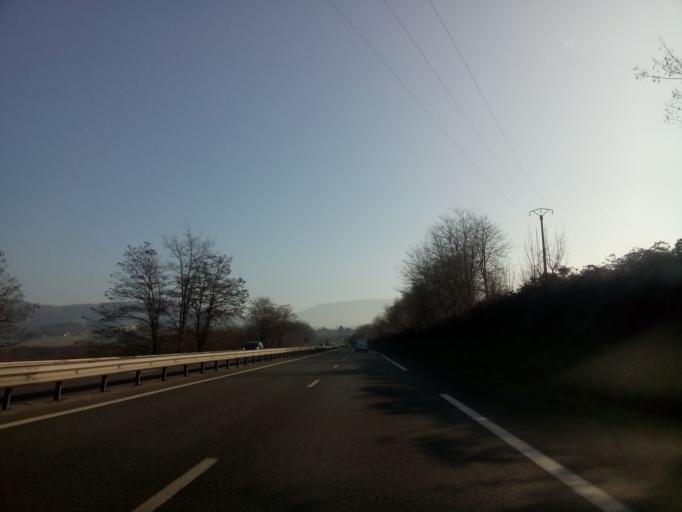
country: FR
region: Rhone-Alpes
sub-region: Departement de la Savoie
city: Le Pont-de-Beauvoisin
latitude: 45.5637
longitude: 5.6798
